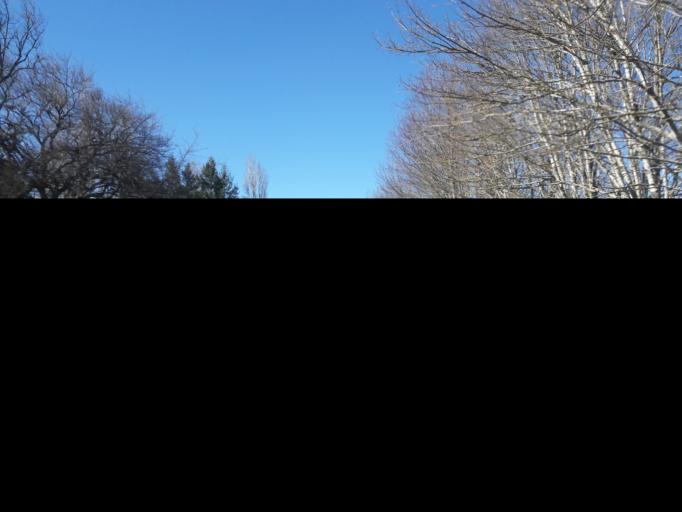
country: CL
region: Araucania
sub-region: Provincia de Malleco
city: Victoria
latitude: -38.2704
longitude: -72.2077
